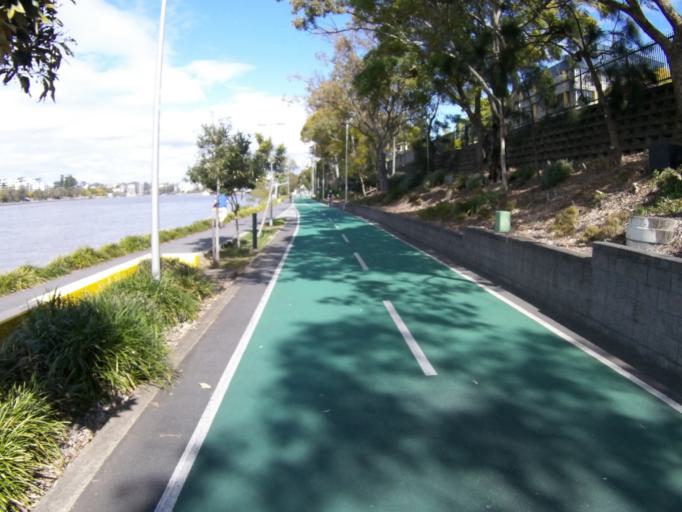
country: AU
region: Queensland
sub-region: Brisbane
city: Milton
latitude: -27.4778
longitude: 153.0005
